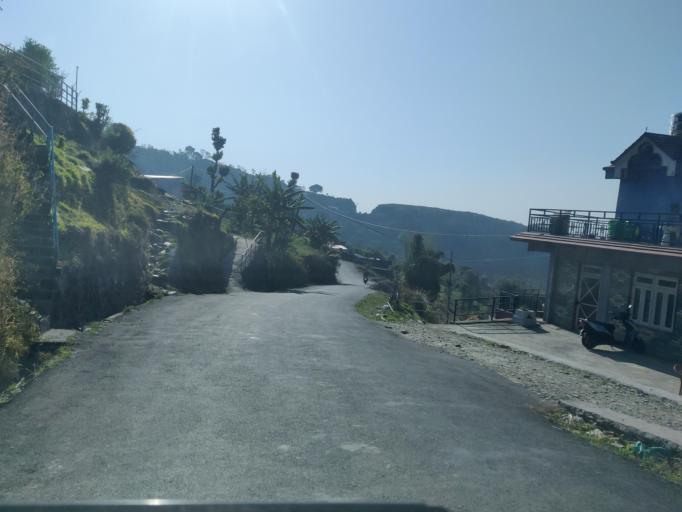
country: NP
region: Western Region
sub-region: Gandaki Zone
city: Pokhara
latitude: 28.2382
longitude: 83.9616
